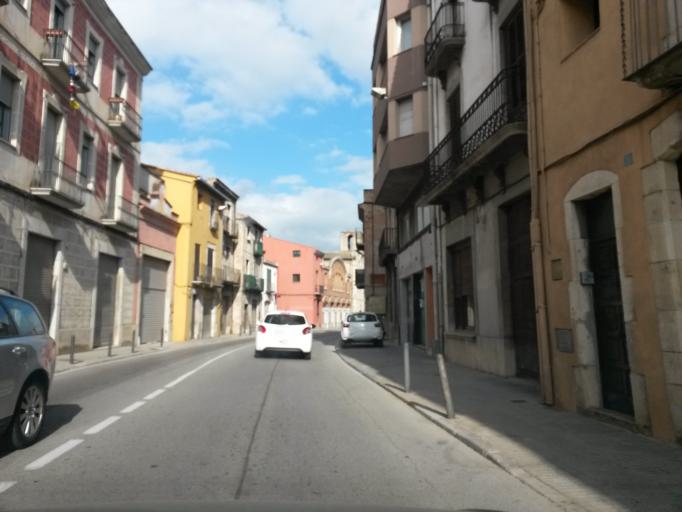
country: ES
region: Catalonia
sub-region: Provincia de Girona
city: Sarria de Ter
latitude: 42.0115
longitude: 2.8253
